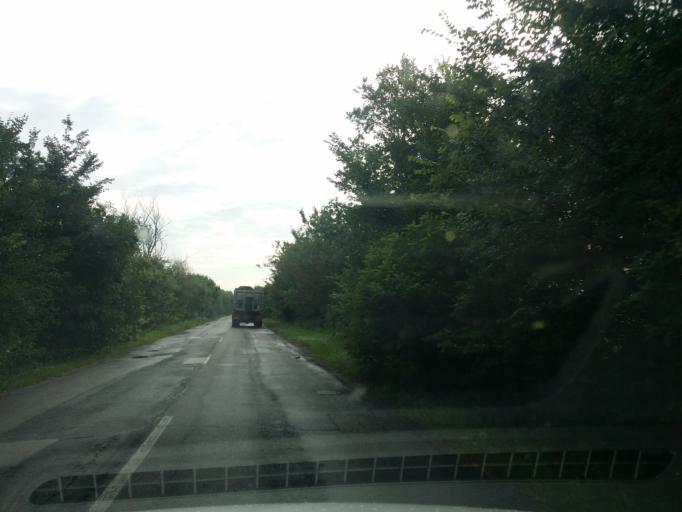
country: HU
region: Heves
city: Poroszlo
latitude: 47.6364
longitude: 20.6280
